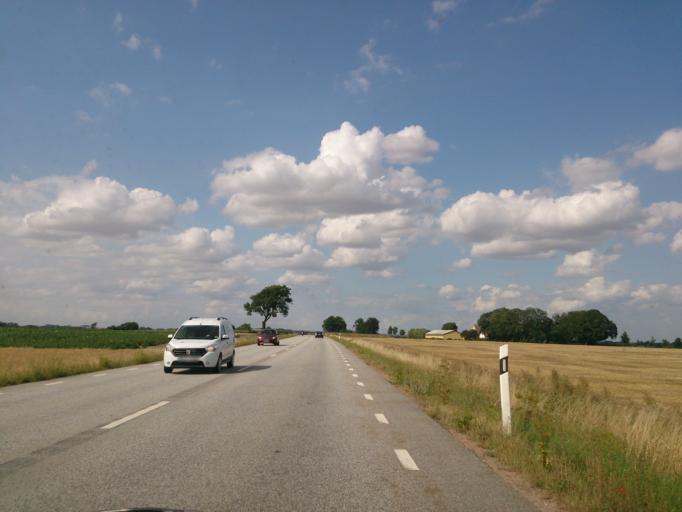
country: SE
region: Skane
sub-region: Kavlinge Kommun
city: Kaevlinge
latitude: 55.7801
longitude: 13.1340
